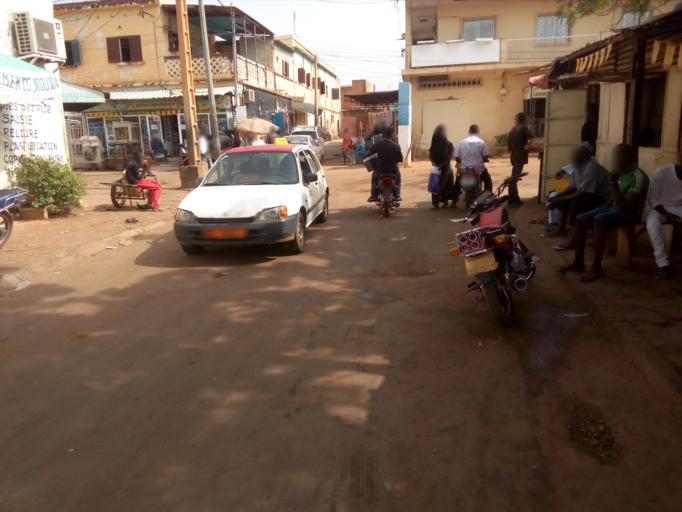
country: NE
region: Niamey
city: Niamey
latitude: 13.5147
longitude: 2.1122
